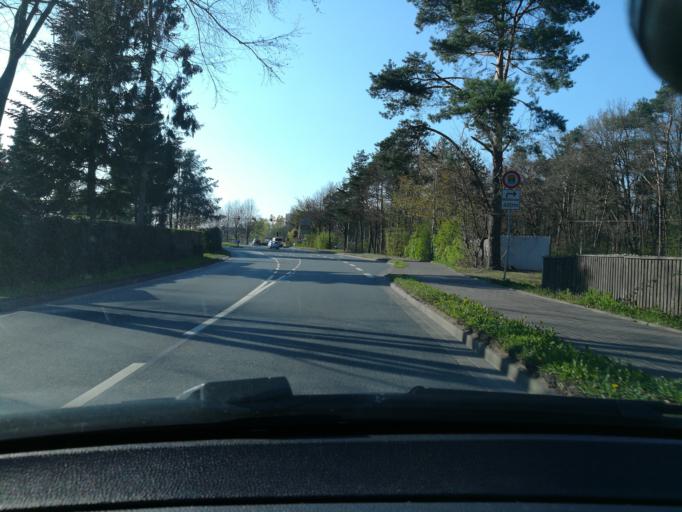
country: DE
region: North Rhine-Westphalia
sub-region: Regierungsbezirk Detmold
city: Verl
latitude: 51.9389
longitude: 8.5713
